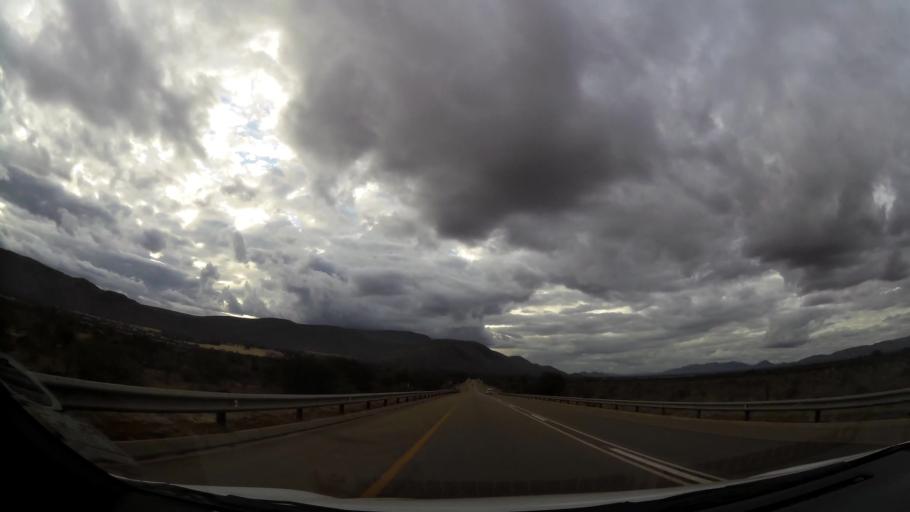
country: ZA
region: Limpopo
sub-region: Waterberg District Municipality
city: Mokopane
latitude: -24.2851
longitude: 28.9812
